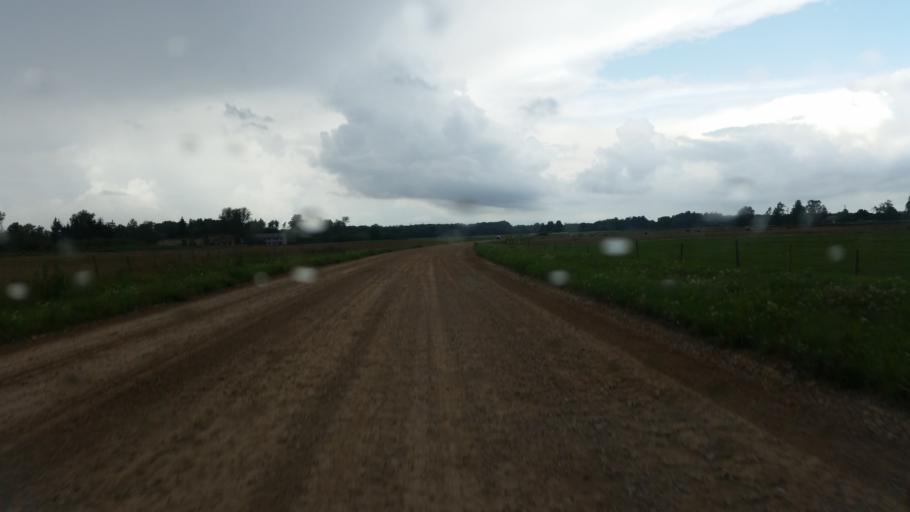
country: LV
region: Vecumnieki
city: Vecumnieki
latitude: 56.4264
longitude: 24.4703
